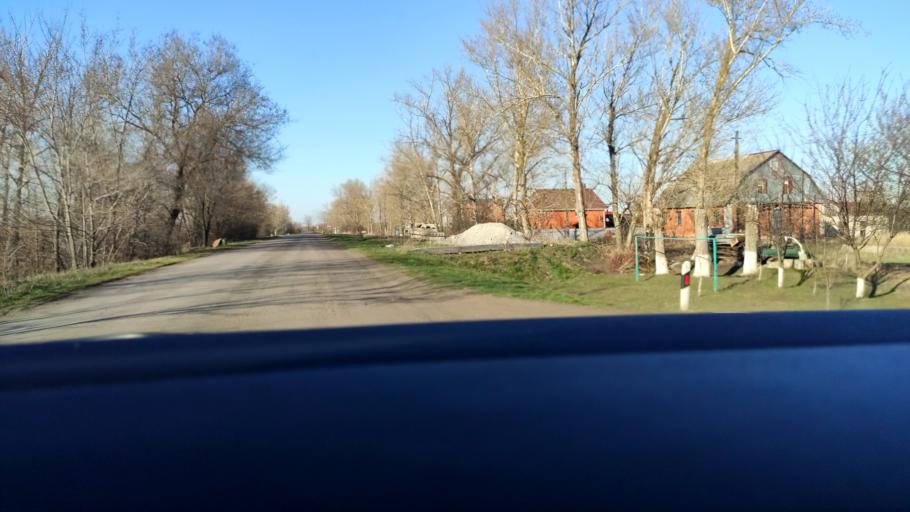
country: RU
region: Voronezj
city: Maslovka
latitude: 51.5125
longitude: 39.2965
